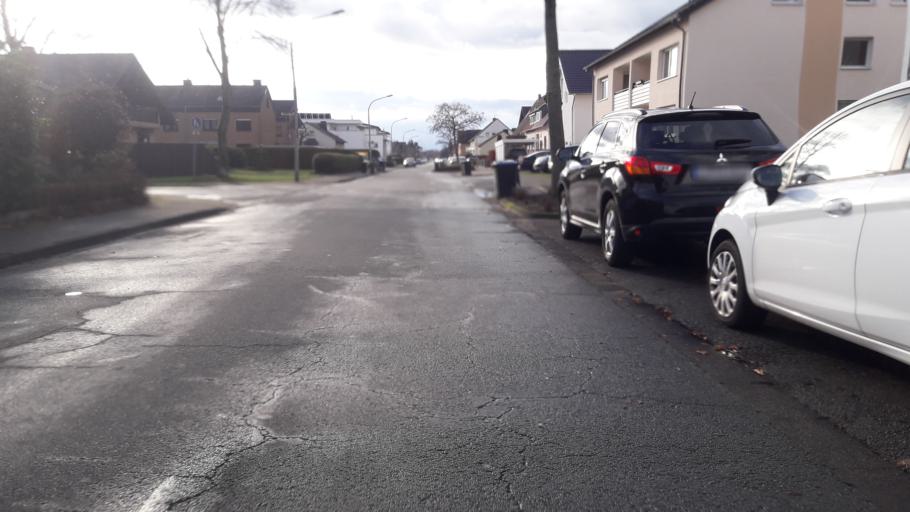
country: DE
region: North Rhine-Westphalia
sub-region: Regierungsbezirk Detmold
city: Paderborn
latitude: 51.7441
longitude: 8.7680
